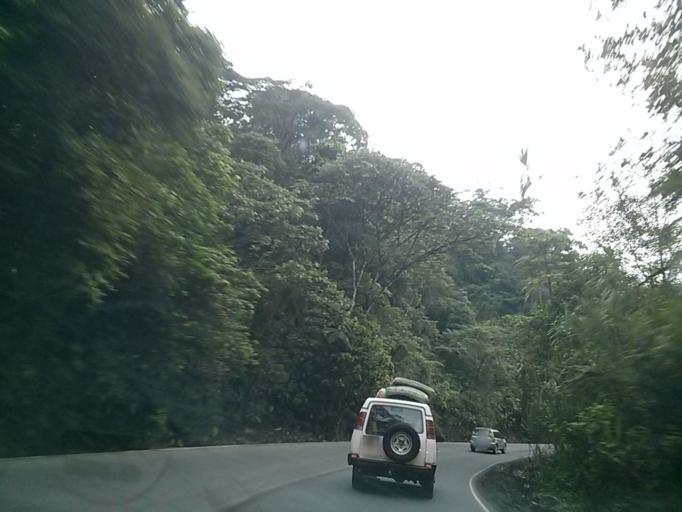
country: CR
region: San Jose
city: Dulce Nombre de Jesus
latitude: 10.1202
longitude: -83.9711
